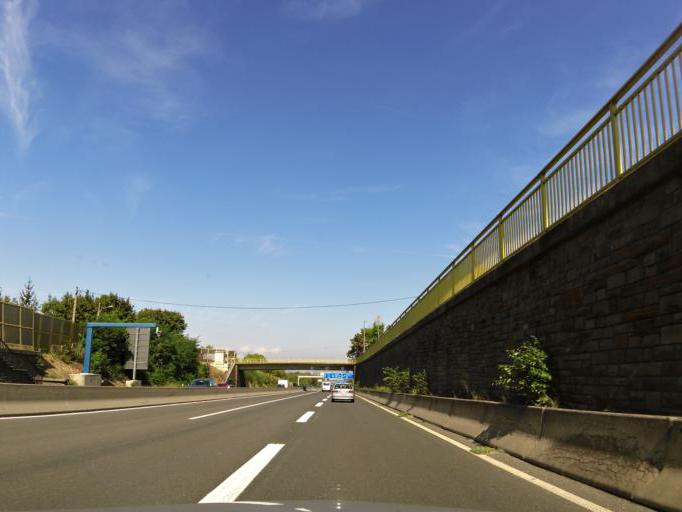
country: DE
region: Rheinland-Pfalz
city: Klein-Winternheim
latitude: 49.9600
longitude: 8.2340
